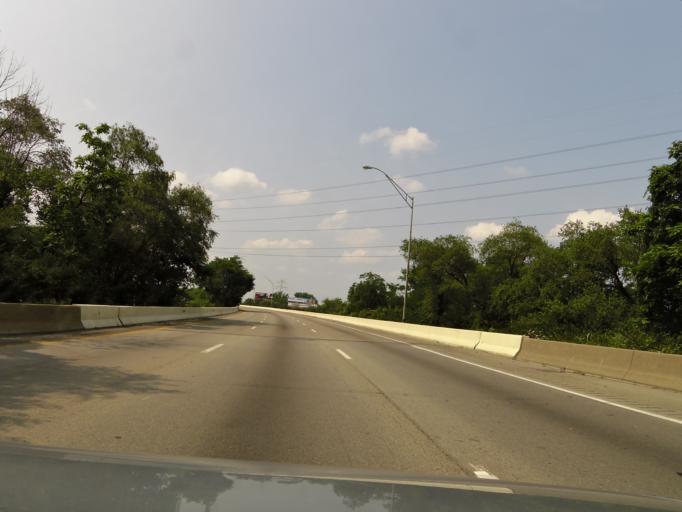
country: US
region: Ohio
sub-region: Hamilton County
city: Reading
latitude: 39.2214
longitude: -84.4481
